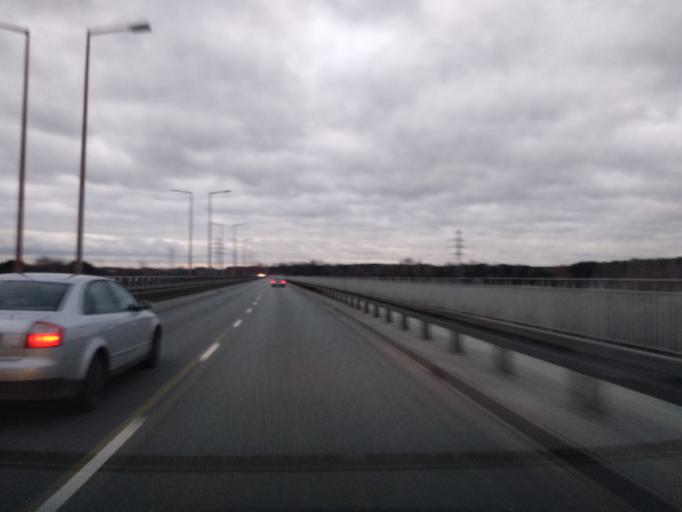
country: PL
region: Greater Poland Voivodeship
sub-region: Konin
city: Konin
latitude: 52.2175
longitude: 18.2309
